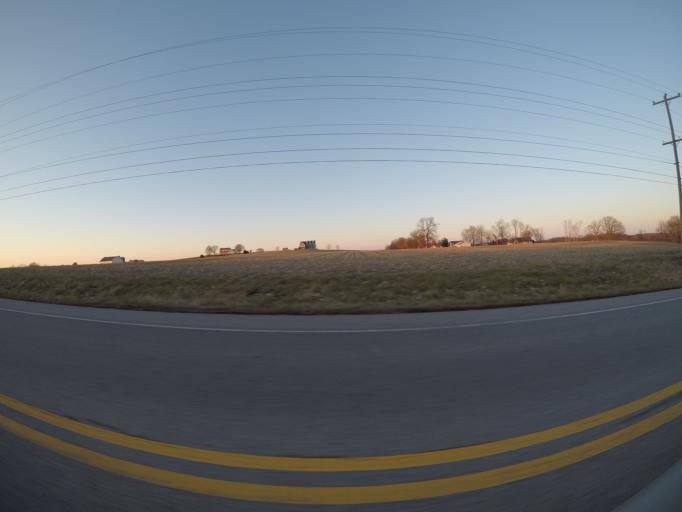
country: US
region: Maryland
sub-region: Cecil County
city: Rising Sun
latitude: 39.6963
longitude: -76.0759
